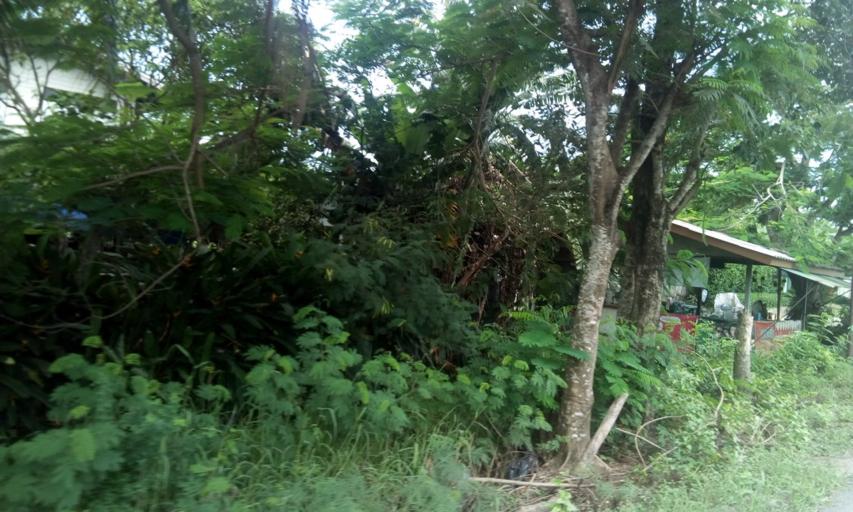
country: TH
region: Pathum Thani
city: Ban Lam Luk Ka
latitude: 14.0087
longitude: 100.8423
